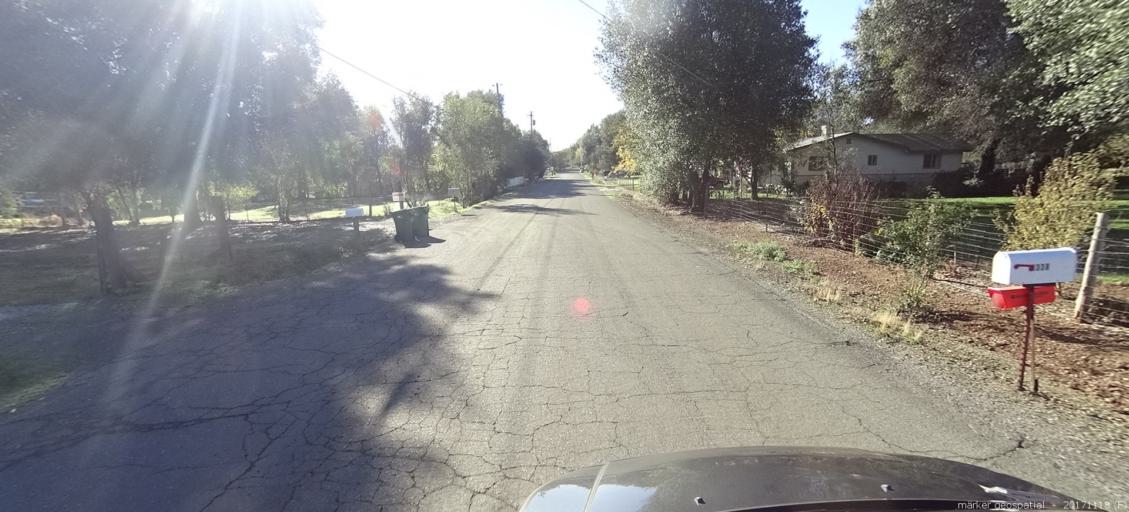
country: US
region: California
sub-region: Shasta County
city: Cottonwood
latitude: 40.3846
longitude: -122.3169
